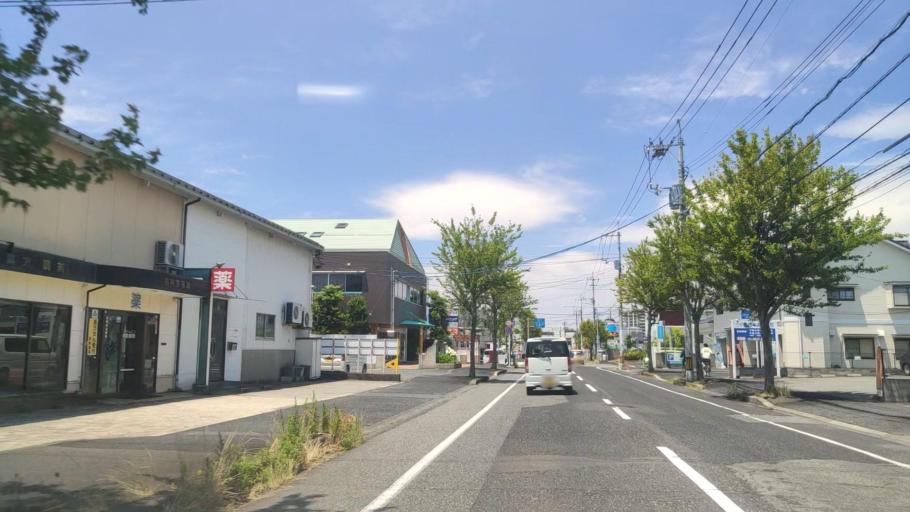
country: JP
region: Tottori
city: Tottori
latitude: 35.4867
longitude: 134.2330
